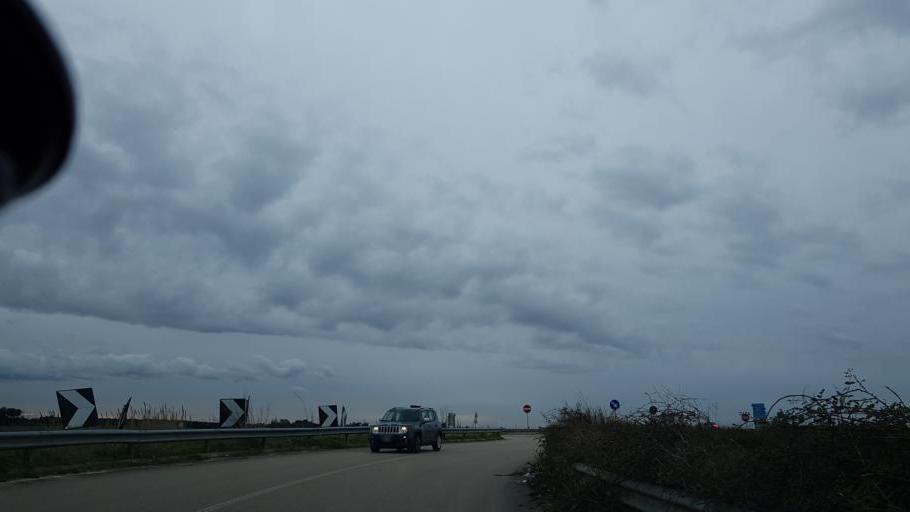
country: IT
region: Apulia
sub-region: Provincia di Brindisi
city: La Rosa
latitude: 40.6172
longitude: 17.9461
